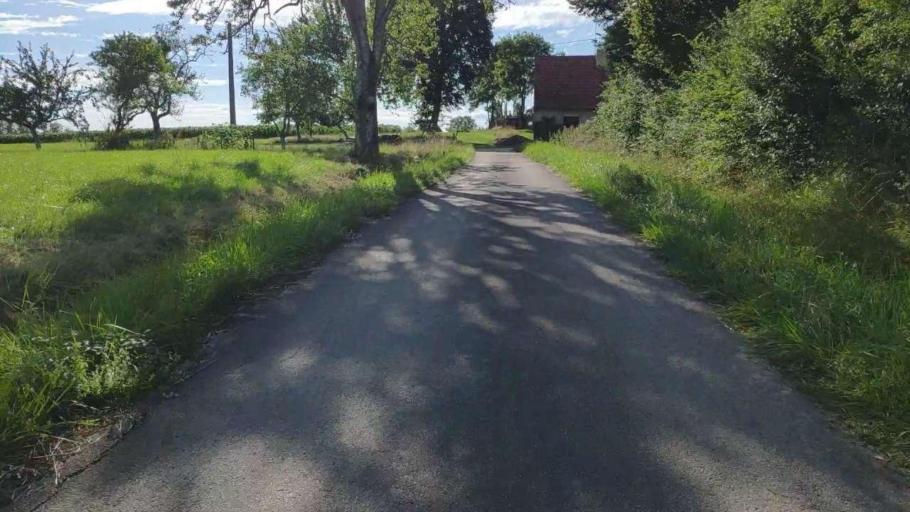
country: FR
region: Franche-Comte
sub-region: Departement du Jura
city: Bletterans
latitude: 46.8253
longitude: 5.4934
